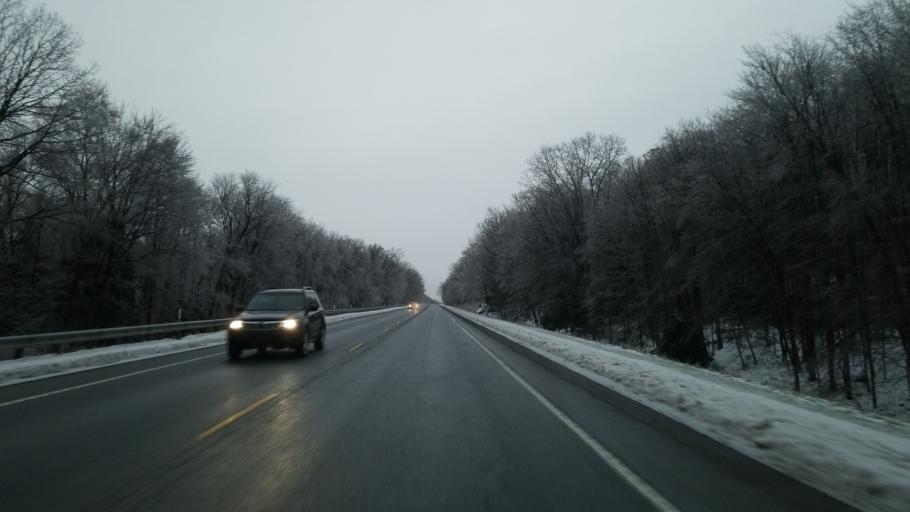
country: US
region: Pennsylvania
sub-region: Clearfield County
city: Curwensville
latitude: 41.0734
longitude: -78.6195
